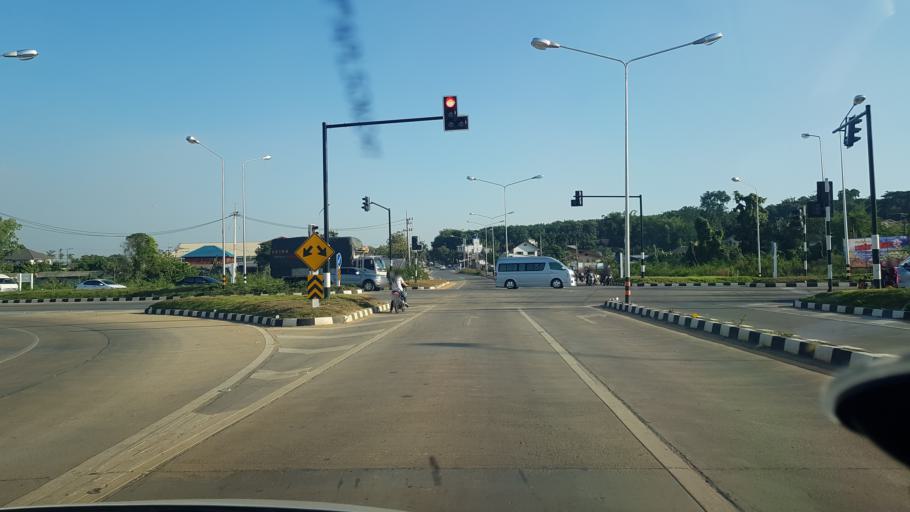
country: TH
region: Chiang Rai
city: Chiang Rai
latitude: 19.9405
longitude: 99.8070
